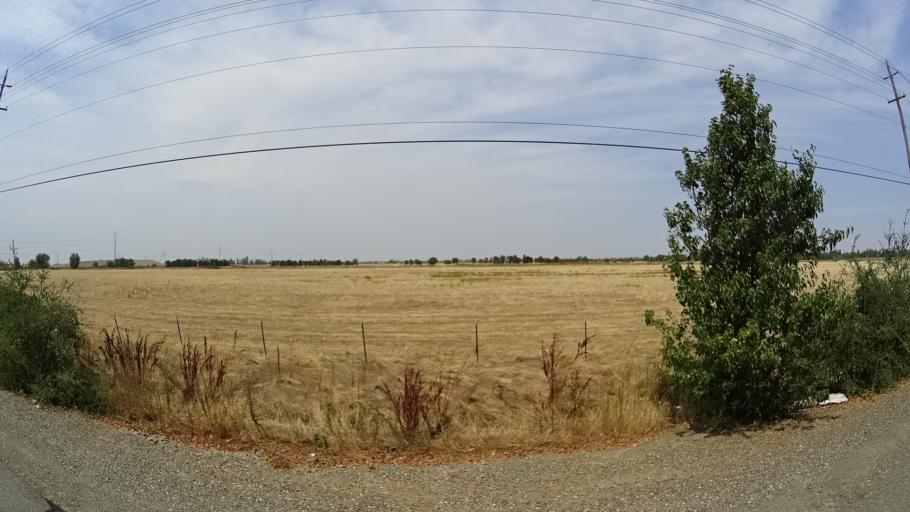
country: US
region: California
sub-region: Sacramento County
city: Laguna
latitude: 38.4345
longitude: -121.4538
